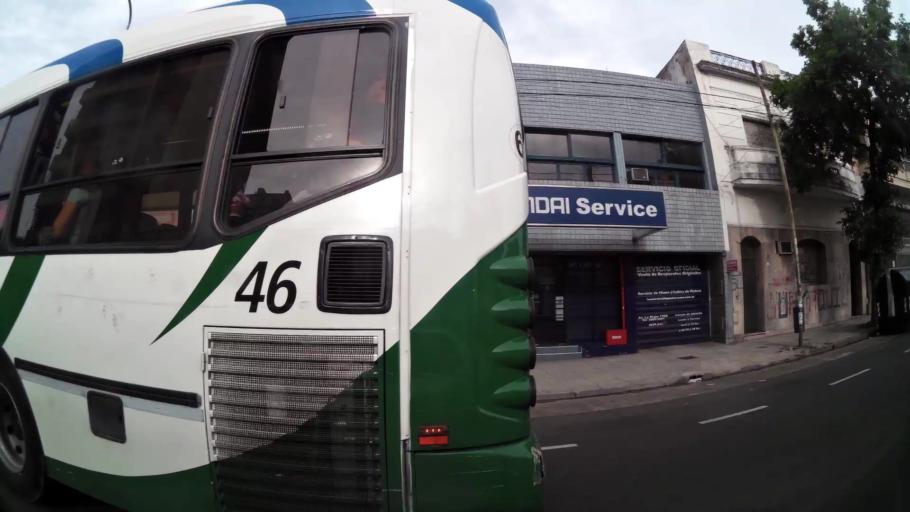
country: AR
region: Buenos Aires F.D.
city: Buenos Aires
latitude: -34.6308
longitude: -58.4259
